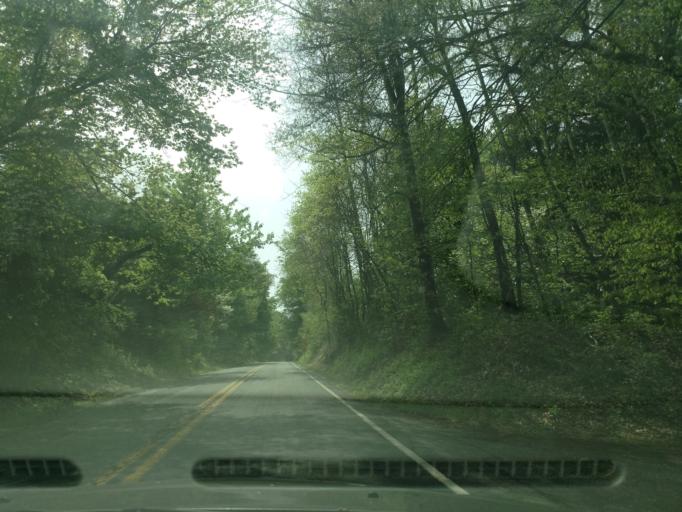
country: US
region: Pennsylvania
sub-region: Chester County
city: Elverson
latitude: 40.1924
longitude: -75.8525
